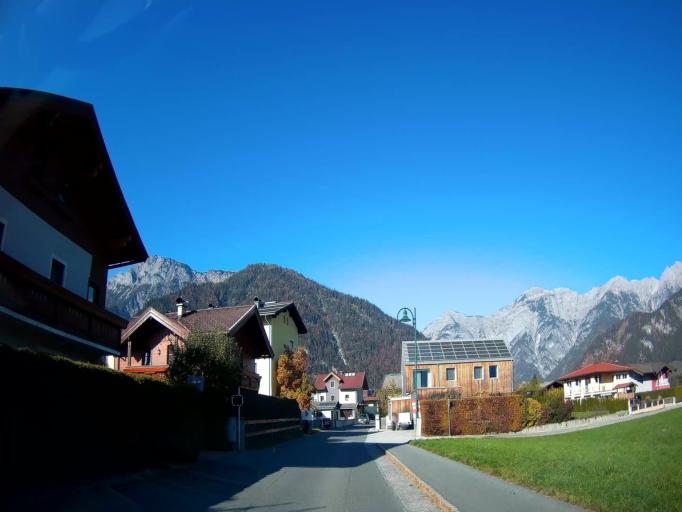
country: AT
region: Salzburg
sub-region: Politischer Bezirk Zell am See
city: Saalfelden am Steinernen Meer
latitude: 47.4435
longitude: 12.8180
